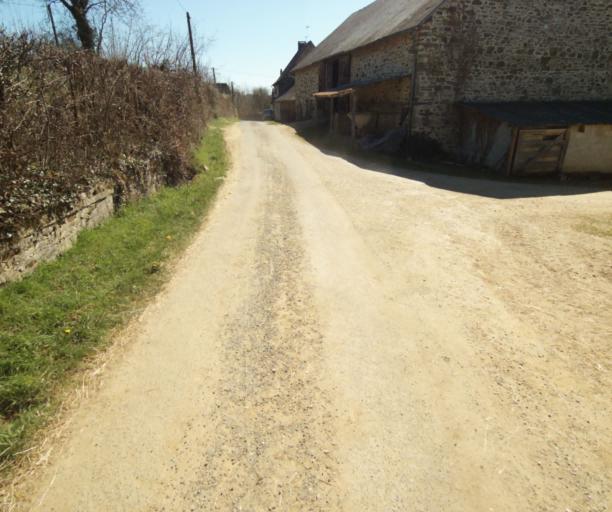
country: FR
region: Limousin
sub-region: Departement de la Correze
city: Chamboulive
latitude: 45.4618
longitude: 1.6687
